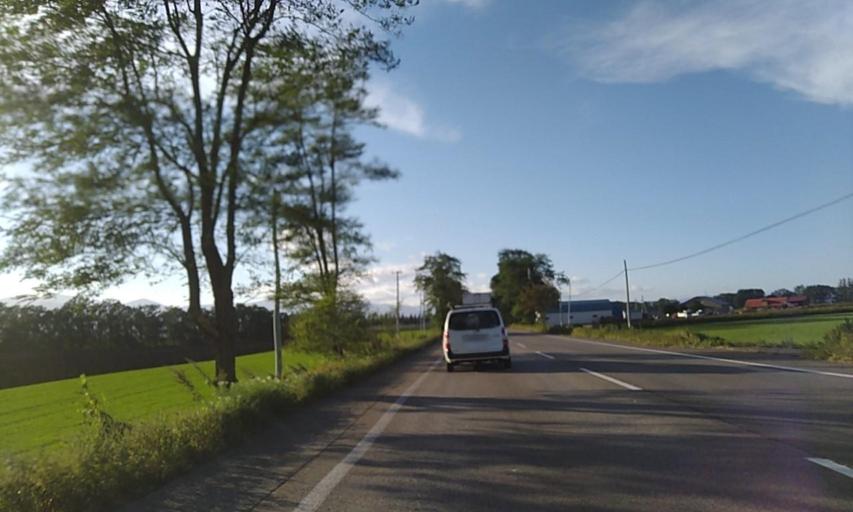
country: JP
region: Hokkaido
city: Obihiro
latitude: 42.9250
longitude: 142.9884
